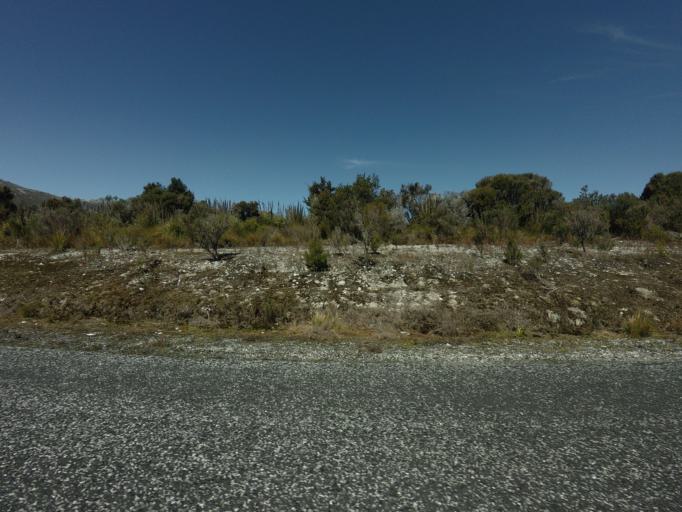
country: AU
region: Tasmania
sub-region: Huon Valley
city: Geeveston
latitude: -42.8353
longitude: 146.1342
